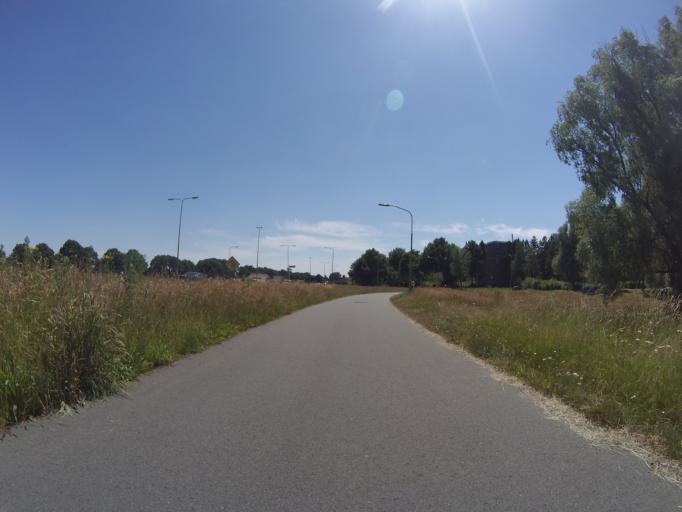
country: NL
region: Drenthe
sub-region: Gemeente Emmen
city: Emmen
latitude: 52.7924
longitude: 6.9496
